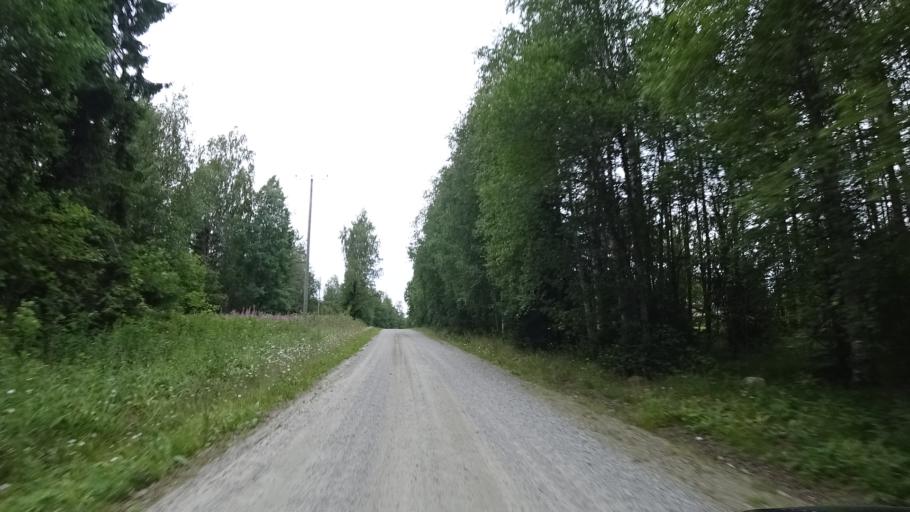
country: FI
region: North Karelia
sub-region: Joensuu
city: Eno
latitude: 63.1762
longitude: 30.5515
